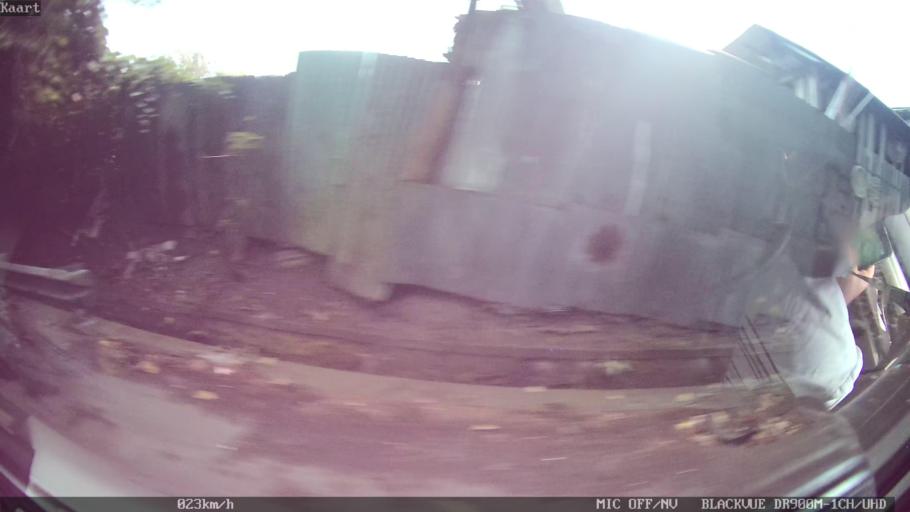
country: ID
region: Bali
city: Banjar Karangsuling
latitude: -8.6058
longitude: 115.1898
